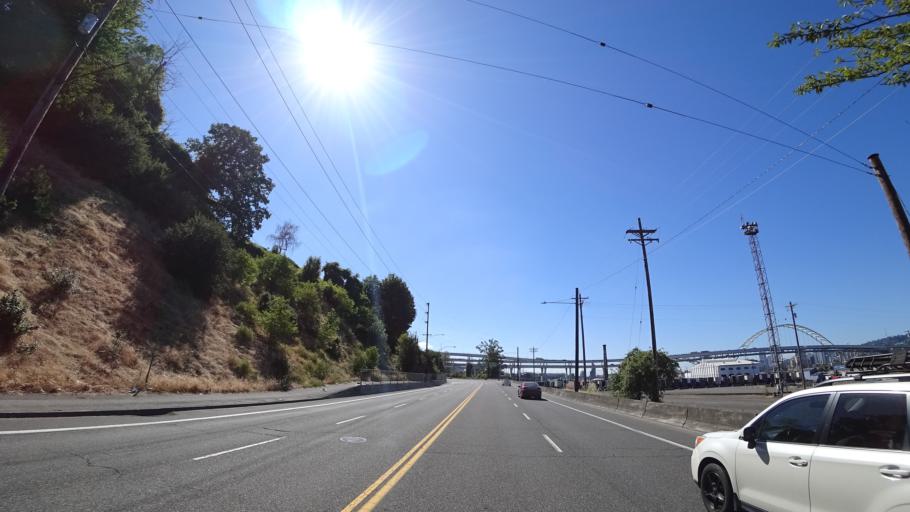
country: US
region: Oregon
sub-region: Multnomah County
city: Portland
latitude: 45.5471
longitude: -122.6836
